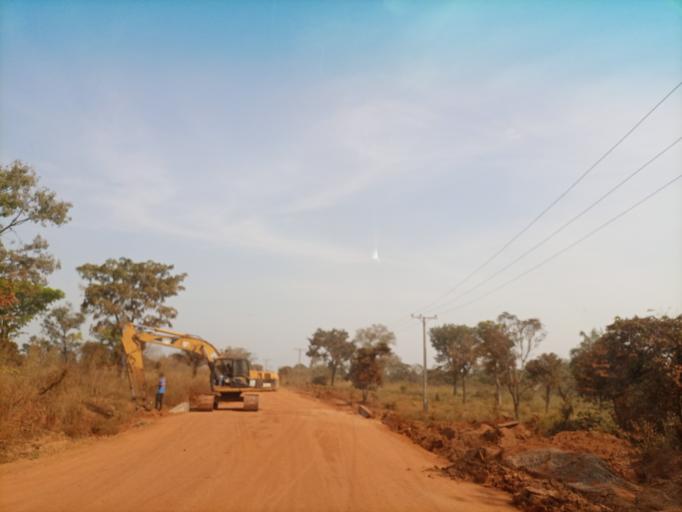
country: NG
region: Enugu
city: Eha Amufu
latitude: 6.6691
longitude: 7.7422
